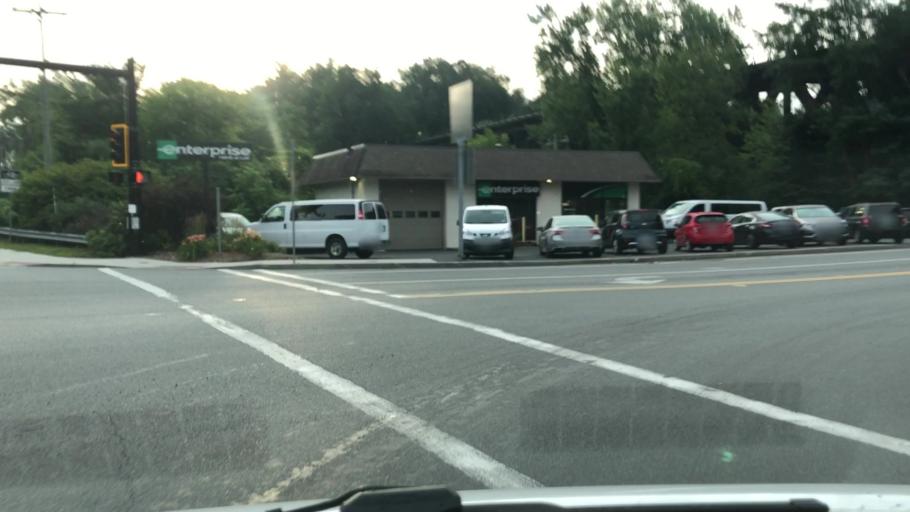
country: US
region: Massachusetts
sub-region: Franklin County
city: Greenfield
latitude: 42.5854
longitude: -72.6128
